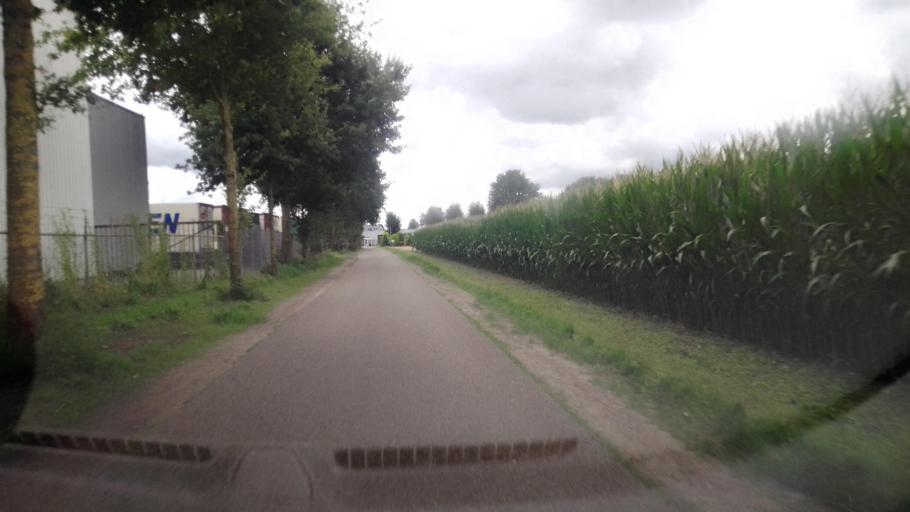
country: NL
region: Limburg
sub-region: Gemeente Peel en Maas
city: Maasbree
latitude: 51.3638
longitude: 6.0597
